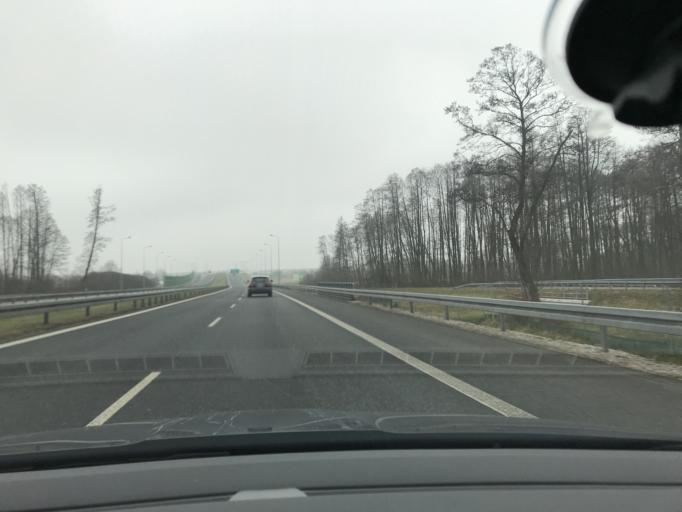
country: PL
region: Lodz Voivodeship
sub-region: Powiat pabianicki
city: Dobron
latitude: 51.6472
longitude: 19.2706
